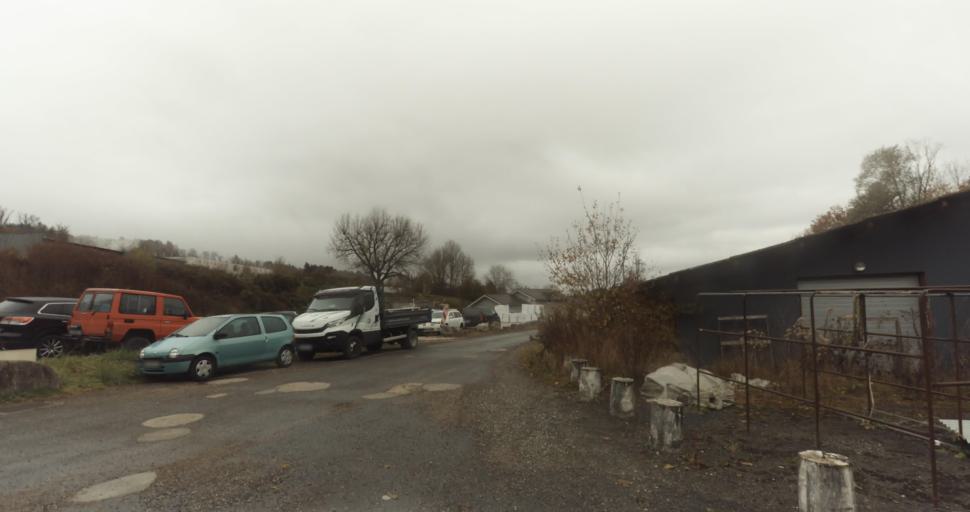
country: FR
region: Rhone-Alpes
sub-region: Departement de la Haute-Savoie
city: Saint-Martin-Bellevue
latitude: 45.9570
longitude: 6.1685
